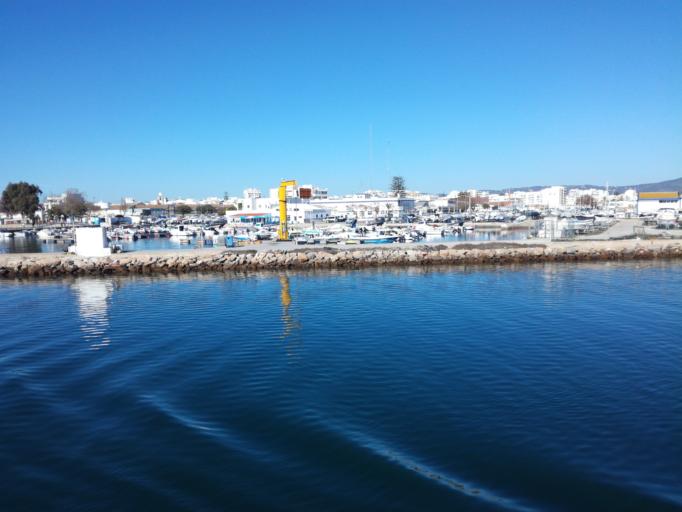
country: PT
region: Faro
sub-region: Olhao
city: Olhao
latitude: 37.0224
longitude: -7.8353
